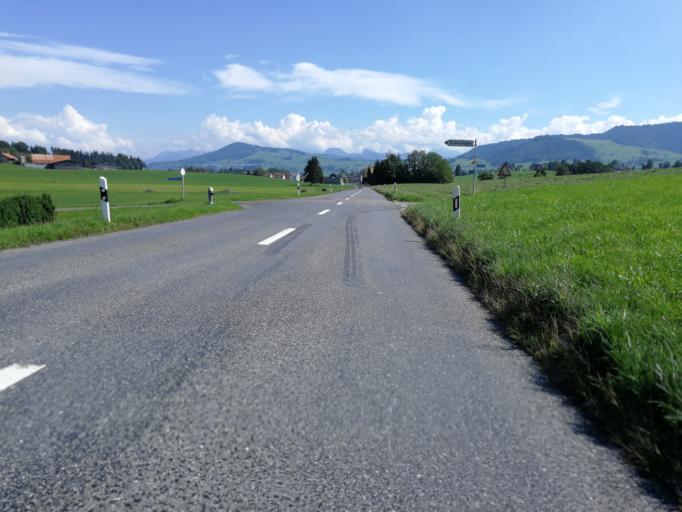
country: CH
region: Zurich
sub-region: Bezirk Horgen
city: Waedenswil / Untermosen-Fuhr
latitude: 47.2103
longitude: 8.6550
